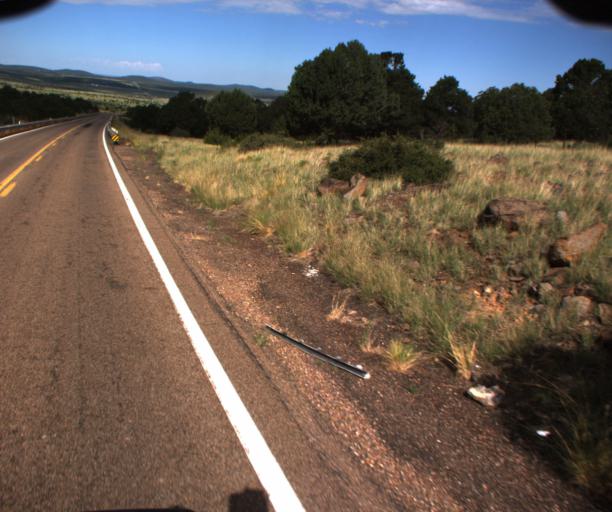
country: US
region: Arizona
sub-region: Apache County
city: Saint Johns
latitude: 34.2665
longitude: -109.6085
